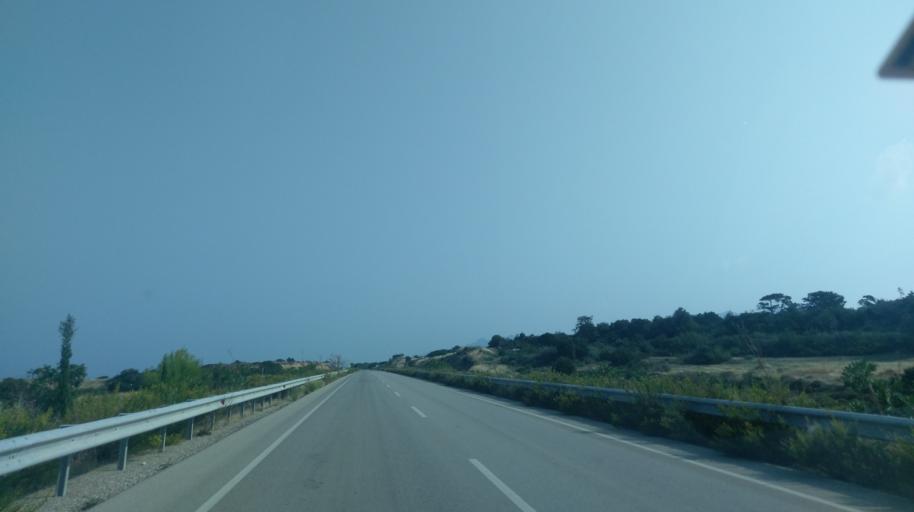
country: CY
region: Ammochostos
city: Trikomo
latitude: 35.4091
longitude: 33.7940
